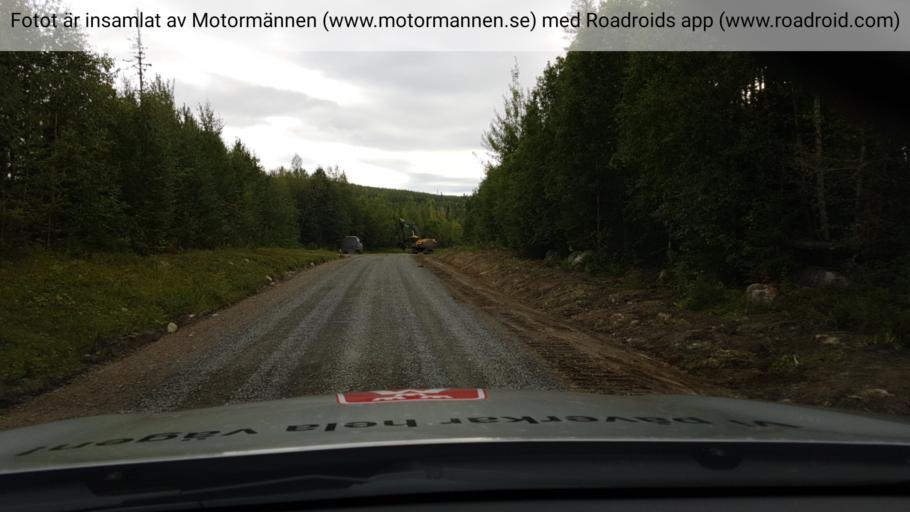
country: SE
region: Jaemtland
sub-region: Ragunda Kommun
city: Hammarstrand
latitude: 62.8736
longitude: 16.0580
